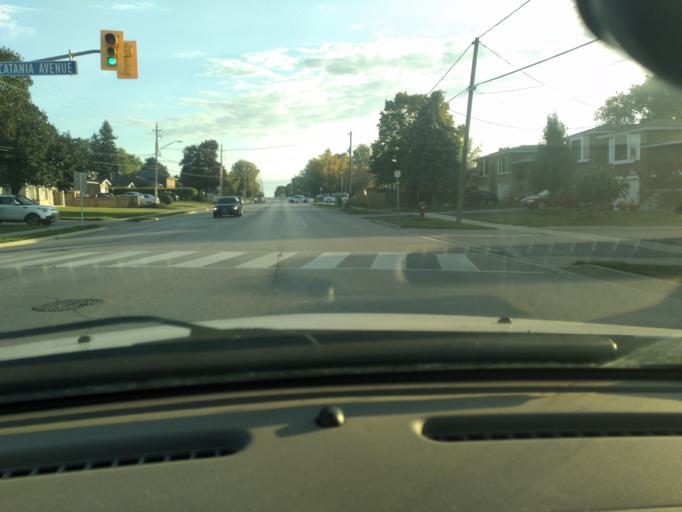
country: CA
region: Ontario
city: Bradford West Gwillimbury
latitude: 44.1038
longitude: -79.5680
